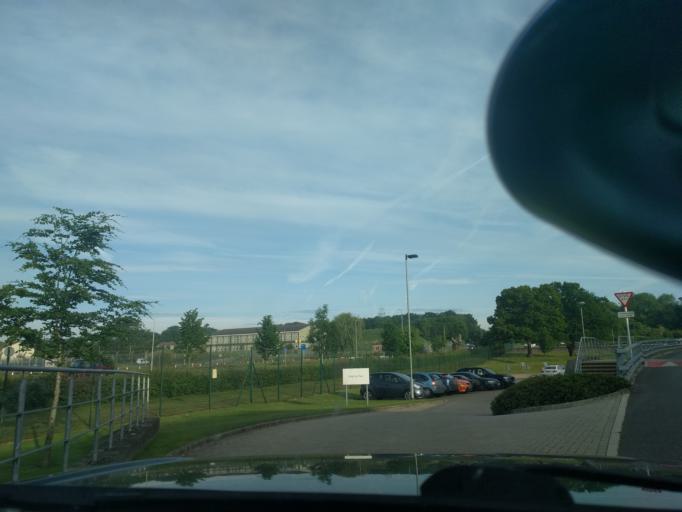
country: GB
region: England
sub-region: Wiltshire
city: Neston
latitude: 51.4202
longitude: -2.2154
